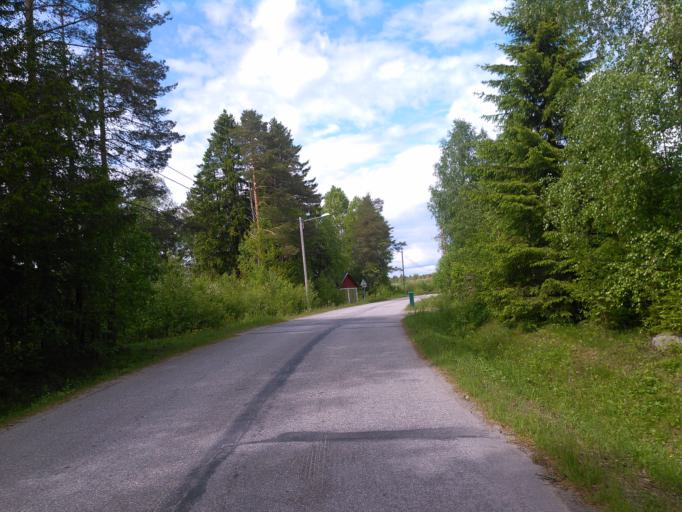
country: SE
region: Vaesterbotten
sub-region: Umea Kommun
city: Ersmark
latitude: 63.8776
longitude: 20.3210
